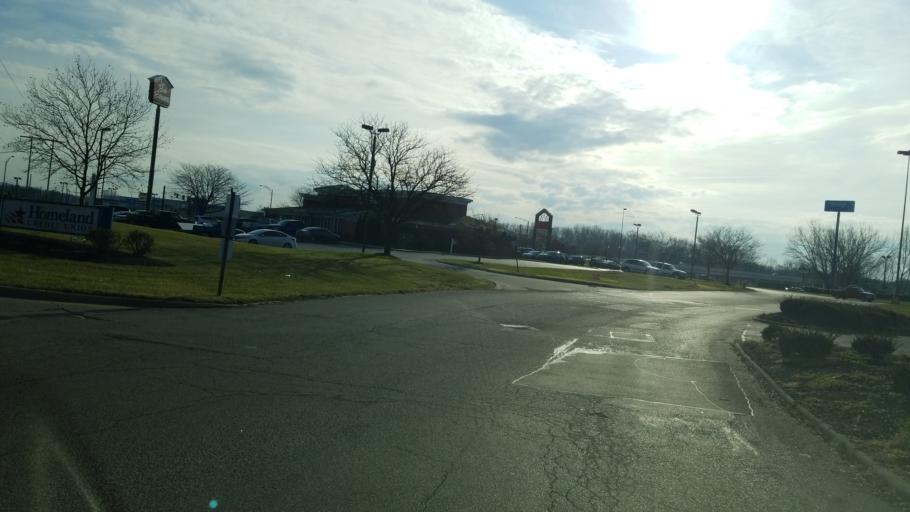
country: US
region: Ohio
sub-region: Ross County
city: Chillicothe
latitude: 39.3468
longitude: -82.9783
